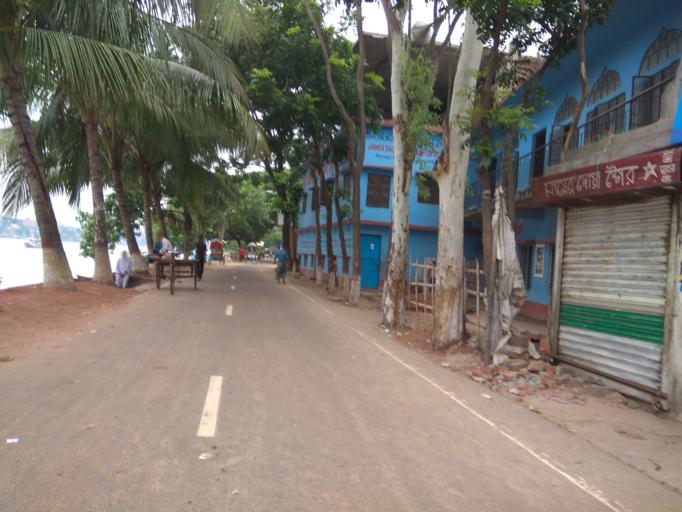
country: BD
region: Dhaka
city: Azimpur
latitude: 23.7088
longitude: 90.3827
